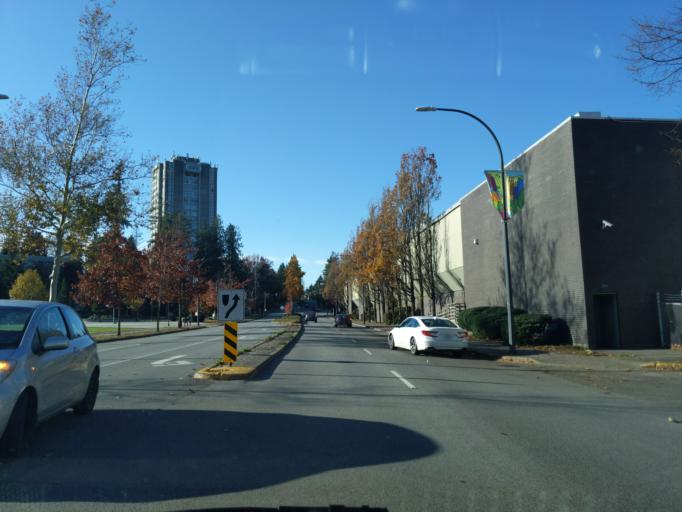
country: CA
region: British Columbia
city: New Westminster
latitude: 49.1852
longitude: -122.8495
